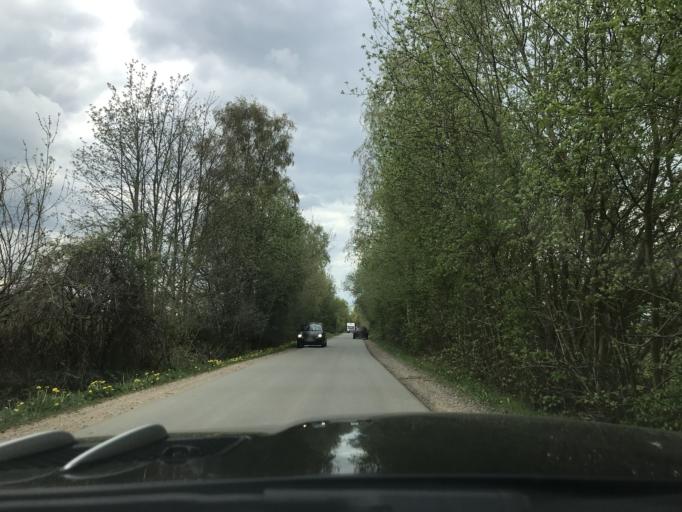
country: DE
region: Schleswig-Holstein
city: Gross Gronau
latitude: 53.7895
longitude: 10.7853
